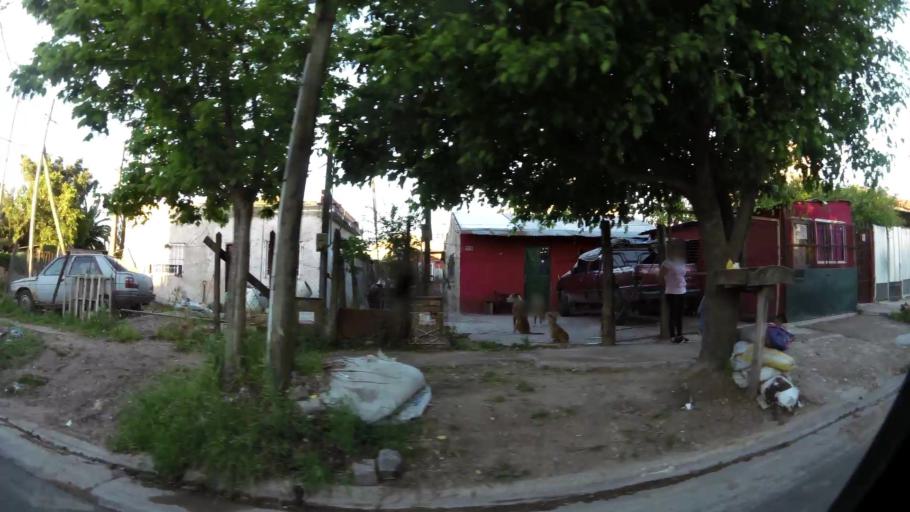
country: AR
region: Buenos Aires
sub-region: Partido de Almirante Brown
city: Adrogue
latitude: -34.7824
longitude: -58.3337
